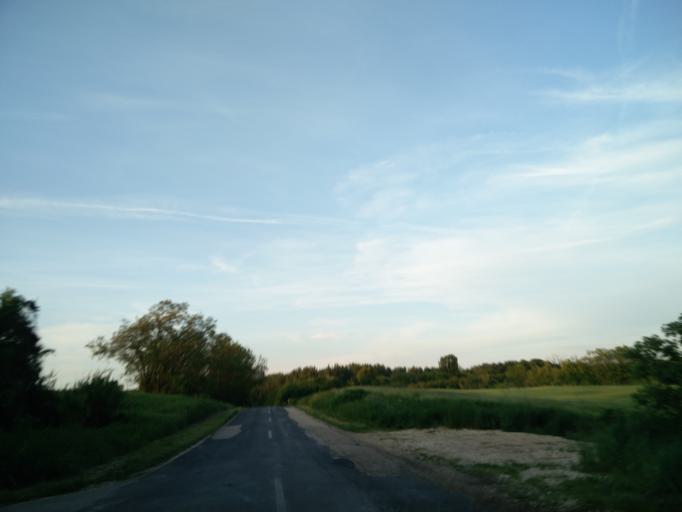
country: HU
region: Fejer
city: Bicske
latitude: 47.4329
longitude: 18.6824
